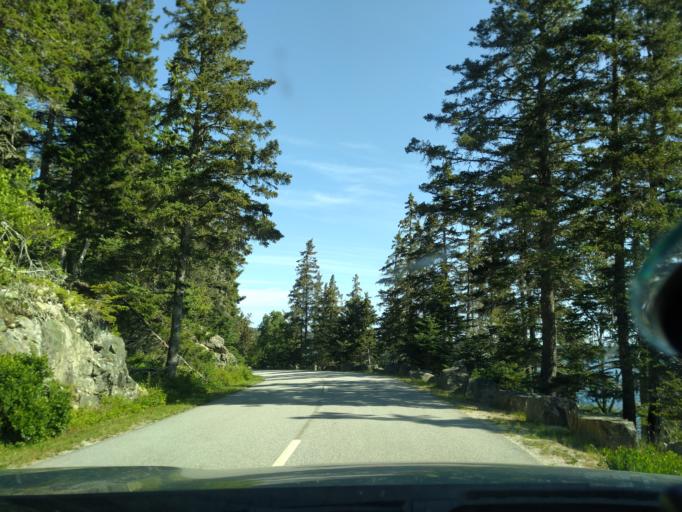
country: US
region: Maine
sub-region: Hancock County
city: Gouldsboro
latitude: 44.3467
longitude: -68.0458
